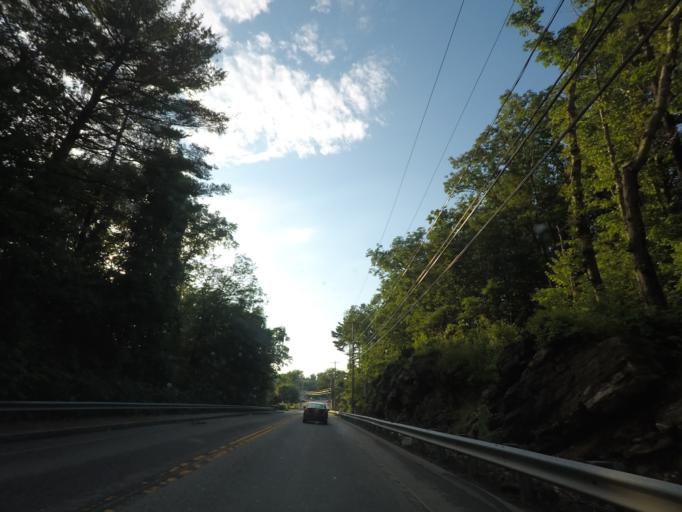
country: US
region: Massachusetts
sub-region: Worcester County
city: Sturbridge
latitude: 42.0946
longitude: -72.0699
